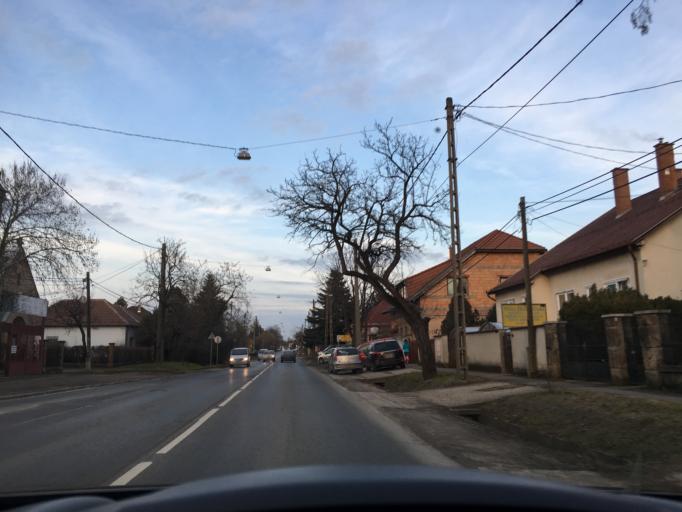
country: HU
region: Budapest
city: Budapest XVII. keruelet
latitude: 47.4844
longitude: 19.2791
